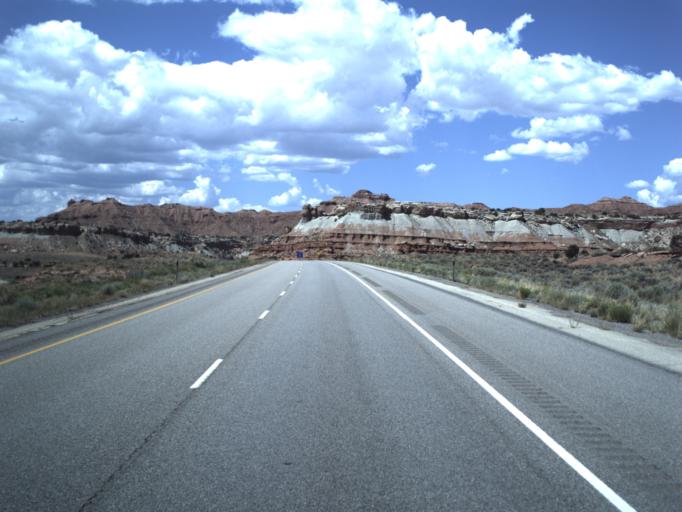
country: US
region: Utah
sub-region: Emery County
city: Ferron
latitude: 38.8403
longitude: -111.0925
